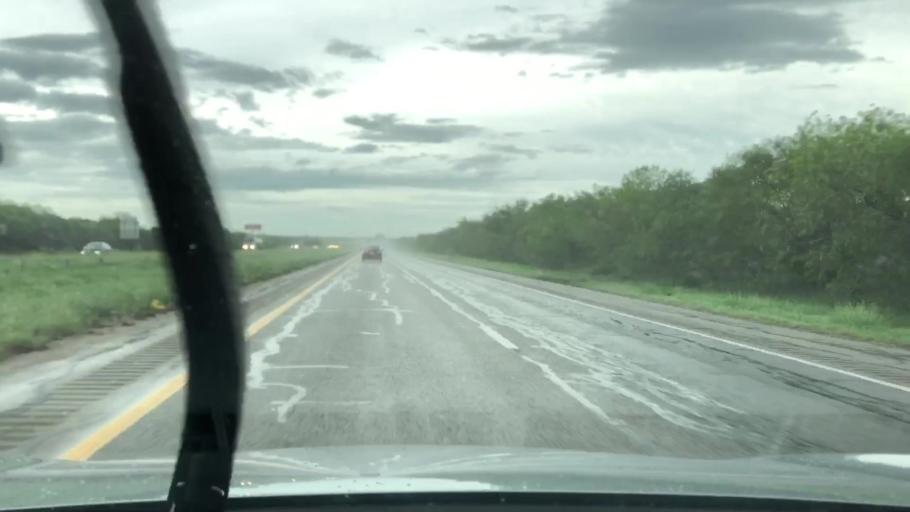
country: US
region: Texas
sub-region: Guadalupe County
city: Seguin
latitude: 29.6038
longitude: -97.8973
